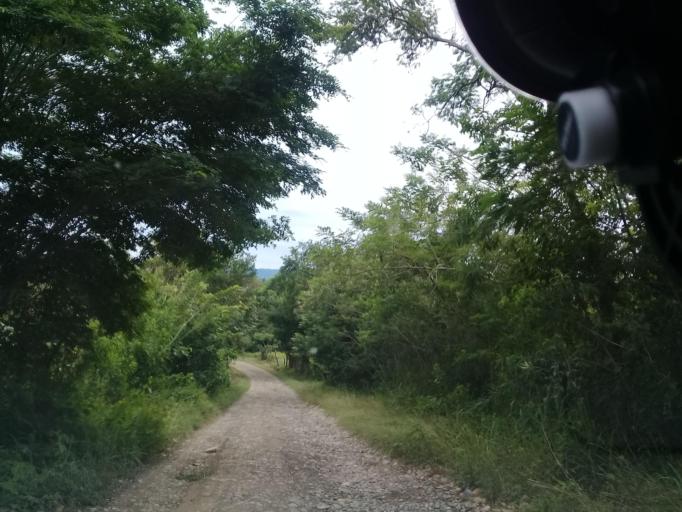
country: MX
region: Hidalgo
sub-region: Huejutla de Reyes
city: Parque de Poblamiento Solidaridad
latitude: 21.1760
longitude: -98.3771
